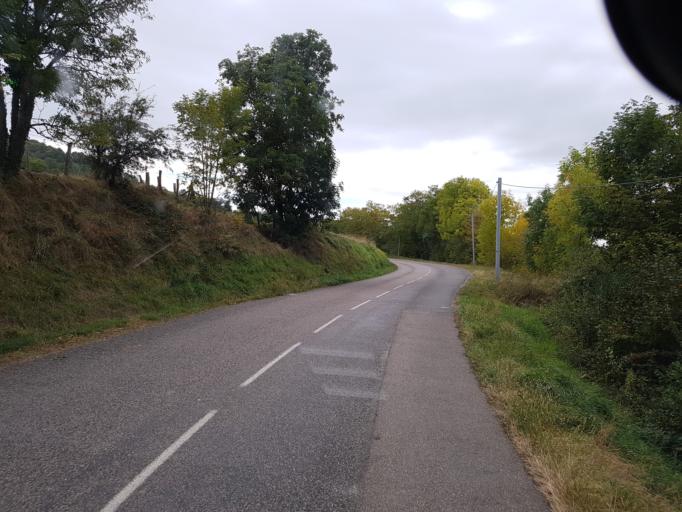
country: FR
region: Rhone-Alpes
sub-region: Departement du Rhone
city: Aveize
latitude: 45.6857
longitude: 4.4528
